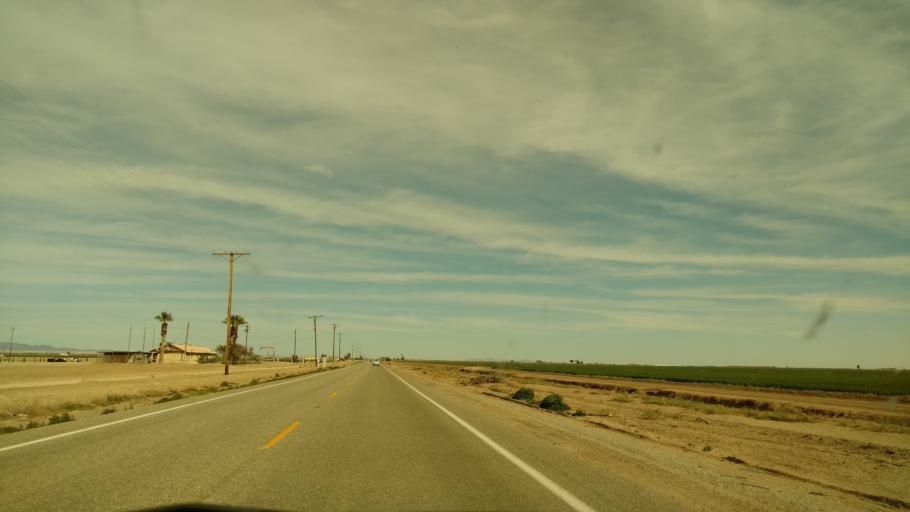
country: US
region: California
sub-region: Imperial County
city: Brawley
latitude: 32.9745
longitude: -115.4000
